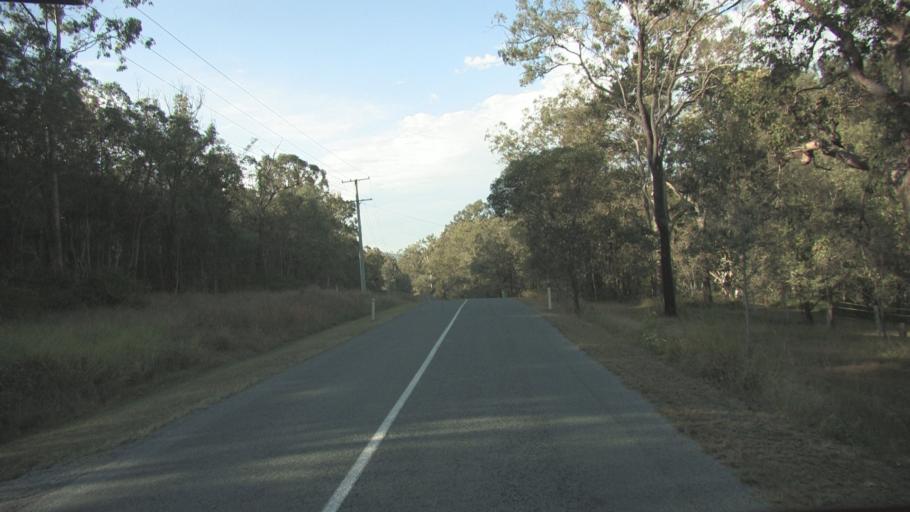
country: AU
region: Queensland
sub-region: Gold Coast
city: Ormeau Hills
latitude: -27.8391
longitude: 153.1662
